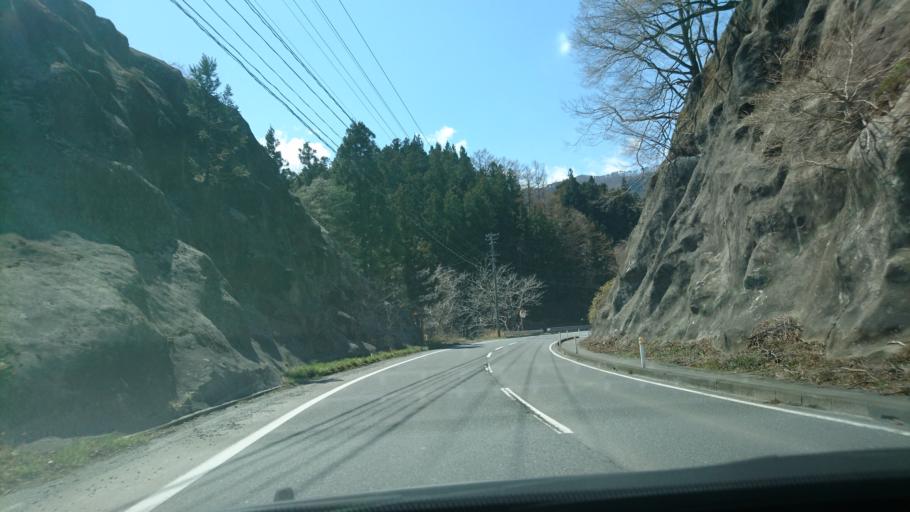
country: JP
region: Iwate
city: Ofunato
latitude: 39.1368
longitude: 141.5837
